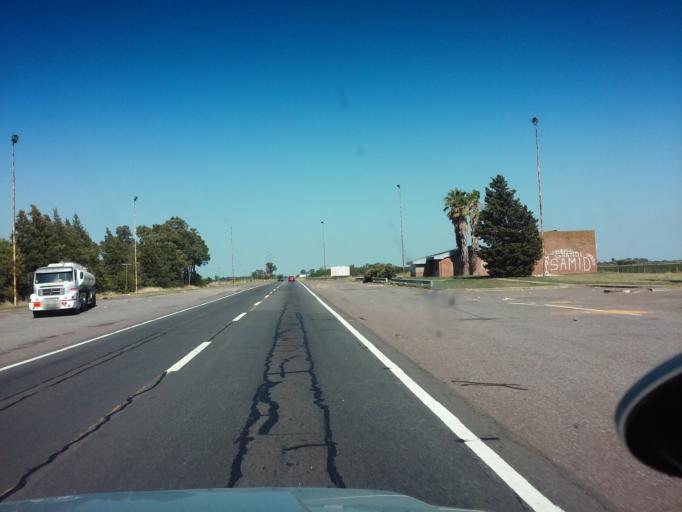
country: AR
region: Buenos Aires
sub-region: Partido de Suipacha
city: Suipacha
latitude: -34.8308
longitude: -59.8251
